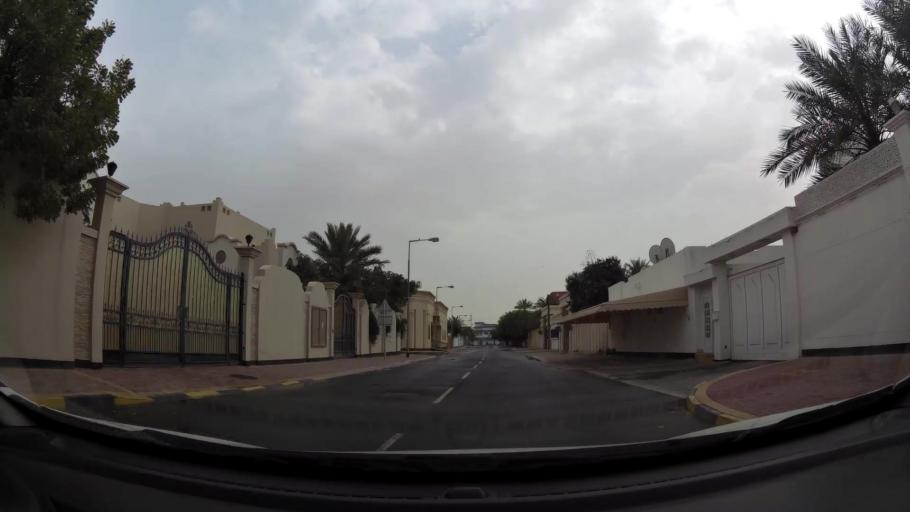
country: BH
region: Northern
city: Ar Rifa'
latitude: 26.1344
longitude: 50.5451
